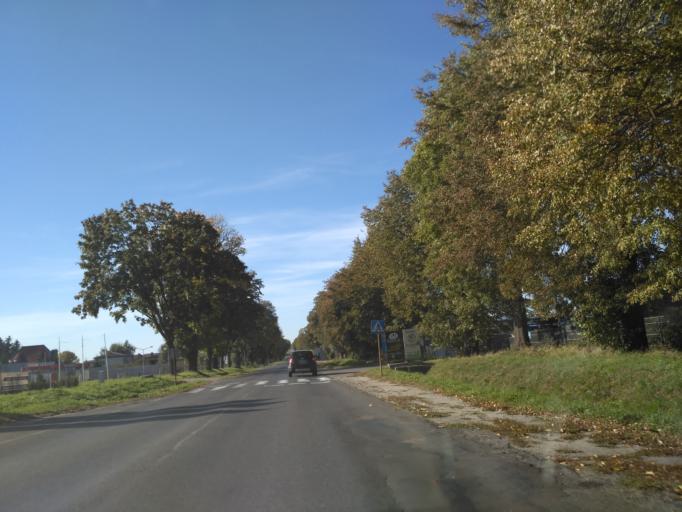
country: PL
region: Lublin Voivodeship
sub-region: Powiat swidnicki
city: Swidnik
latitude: 51.2109
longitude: 22.6479
